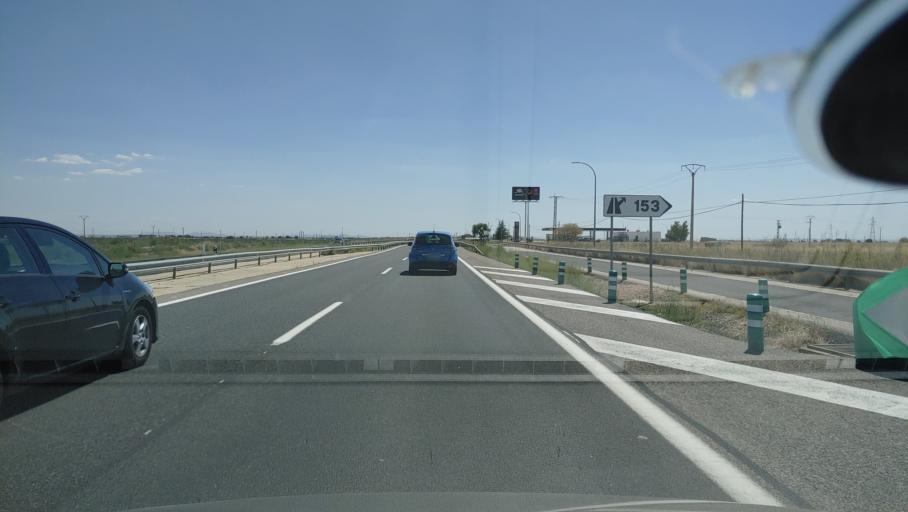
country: ES
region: Castille-La Mancha
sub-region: Provincia de Ciudad Real
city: Villarta de San Juan
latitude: 39.1831
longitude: -3.3986
